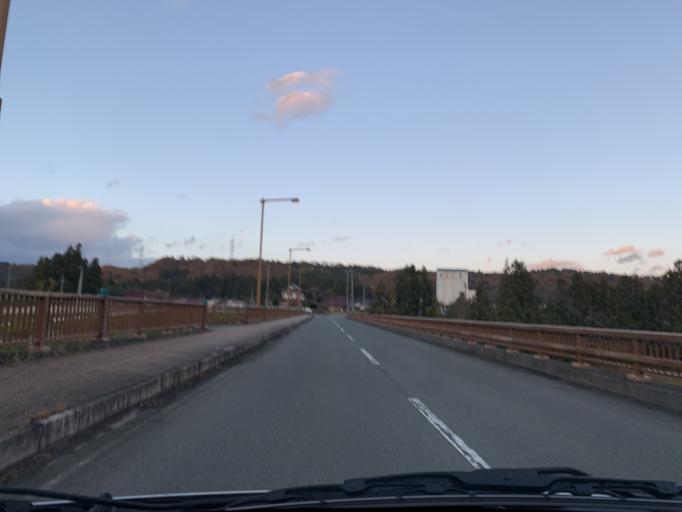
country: JP
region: Iwate
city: Ichinoseki
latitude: 39.0166
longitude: 141.0901
